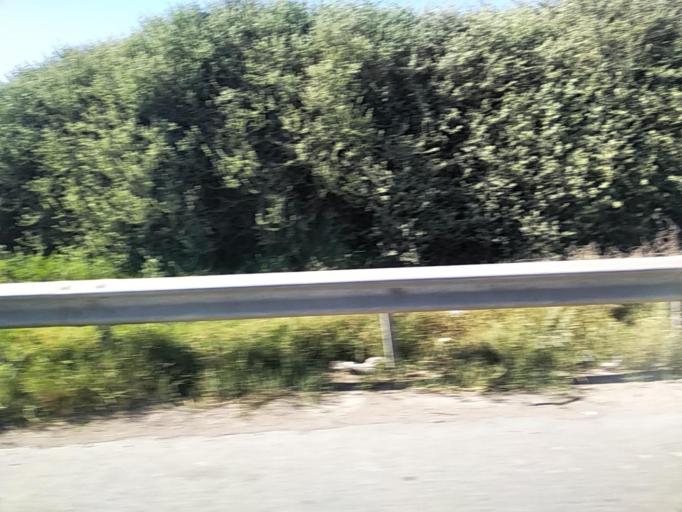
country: CL
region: Atacama
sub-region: Provincia de Copiapo
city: Copiapo
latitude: -27.3122
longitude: -70.4100
